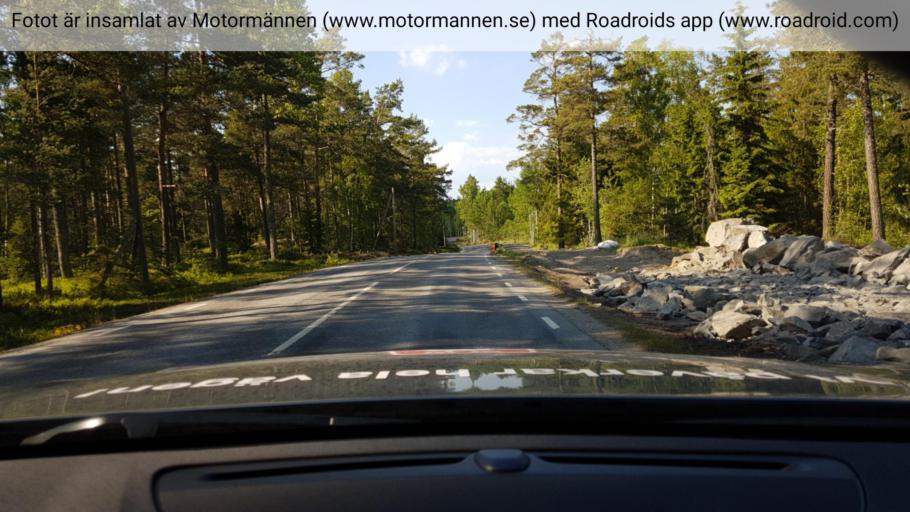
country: SE
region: Stockholm
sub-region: Varmdo Kommun
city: Mortnas
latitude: 59.2706
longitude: 18.4260
